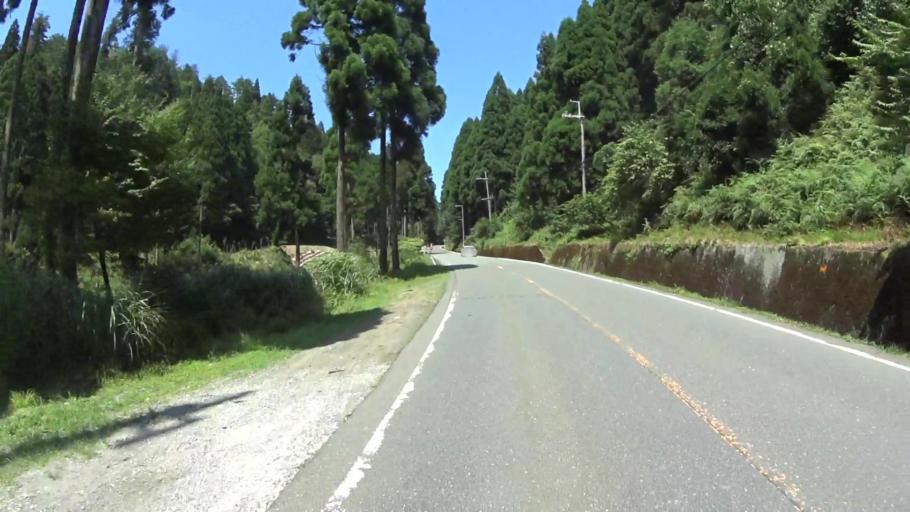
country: JP
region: Fukui
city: Obama
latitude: 35.3842
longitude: 135.9254
